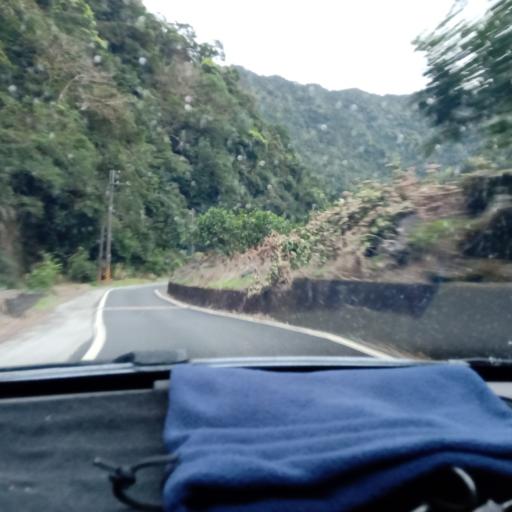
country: TW
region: Taiwan
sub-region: Yilan
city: Yilan
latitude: 24.8089
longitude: 121.7032
